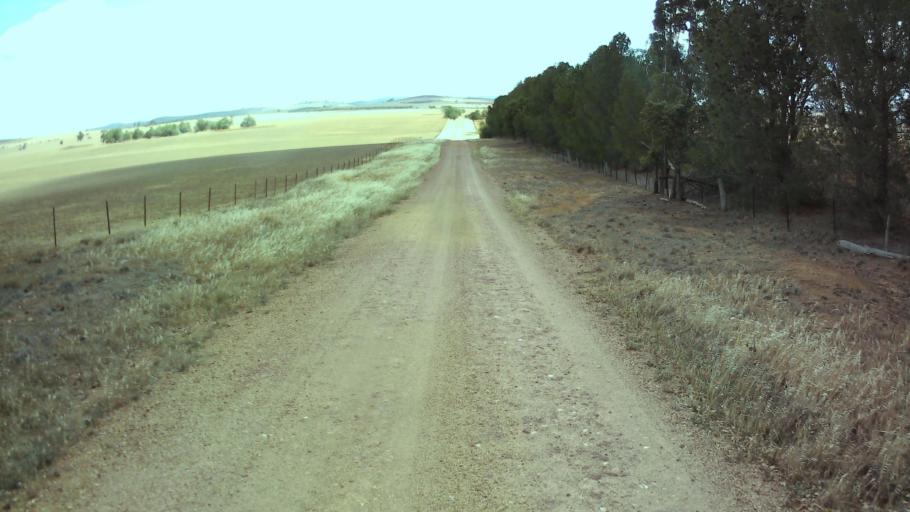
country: AU
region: New South Wales
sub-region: Weddin
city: Grenfell
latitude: -33.9951
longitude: 148.3141
